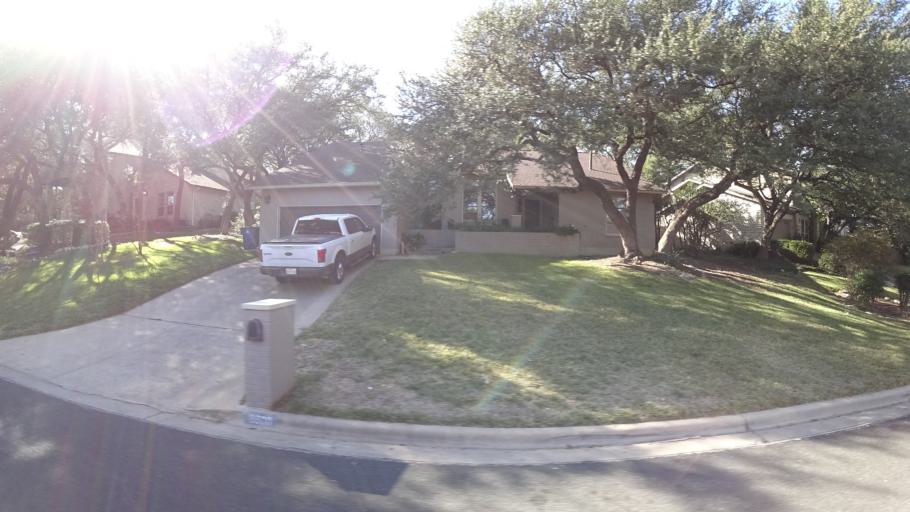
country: US
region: Texas
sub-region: Williamson County
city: Jollyville
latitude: 30.3832
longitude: -97.7593
